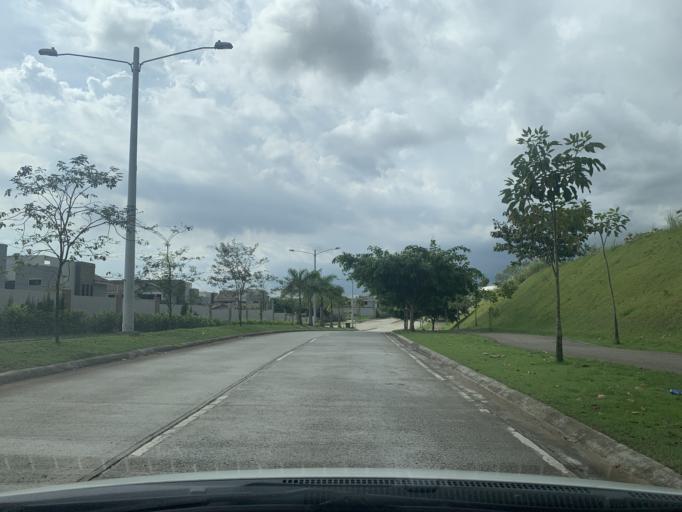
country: PA
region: Panama
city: San Miguelito
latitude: 9.0895
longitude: -79.4662
